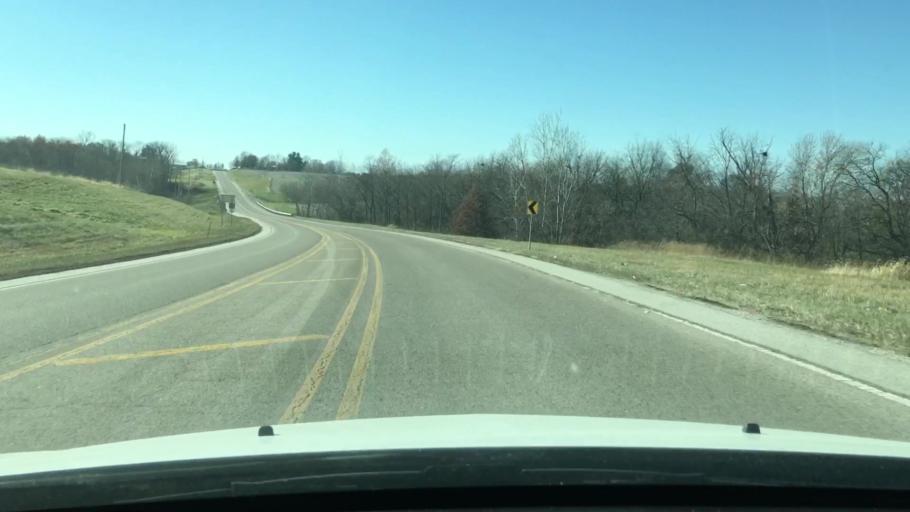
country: US
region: Illinois
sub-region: Pike County
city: Pittsfield
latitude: 39.6043
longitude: -90.8755
